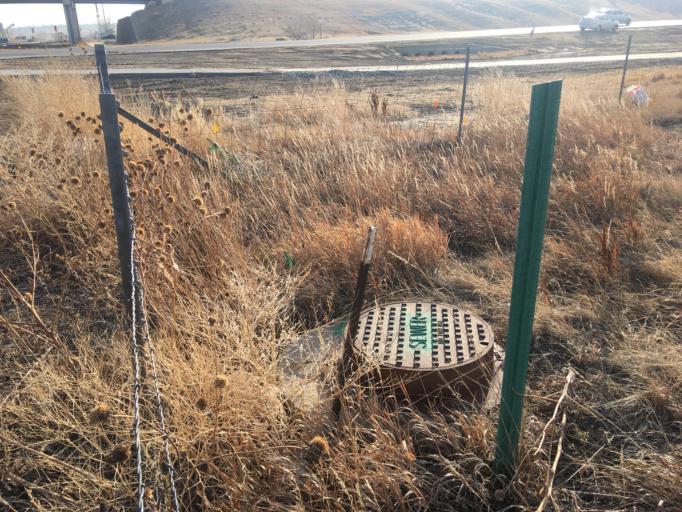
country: US
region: Colorado
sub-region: Boulder County
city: Lafayette
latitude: 39.9600
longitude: -105.0874
